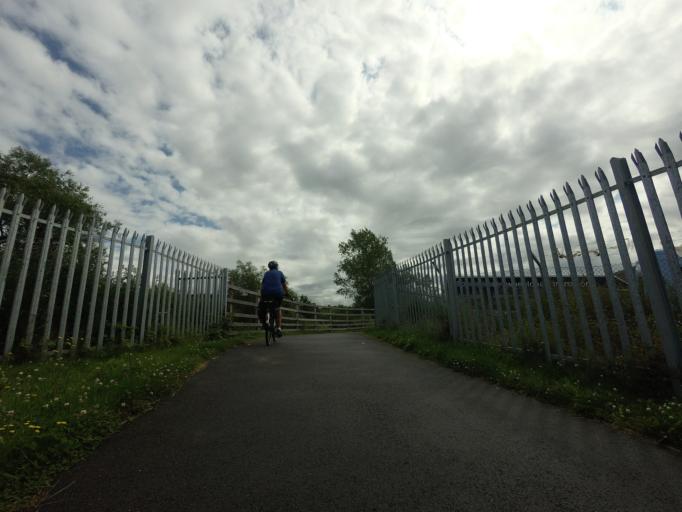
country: GB
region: Scotland
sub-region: Moray
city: Elgin
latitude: 57.6515
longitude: -3.2916
